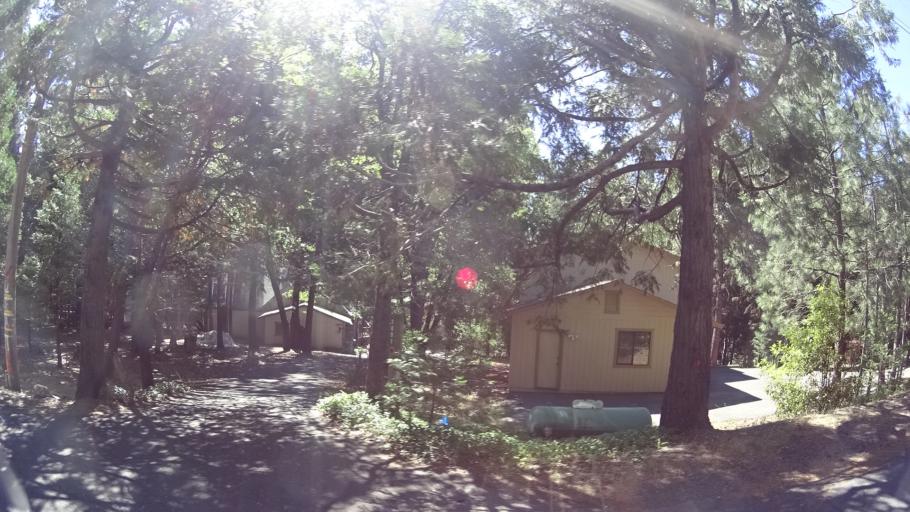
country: US
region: California
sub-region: Calaveras County
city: Arnold
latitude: 38.2504
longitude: -120.3647
